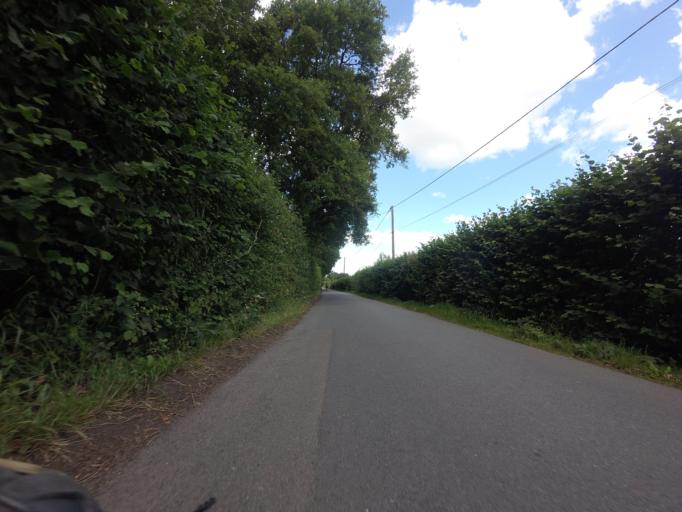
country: GB
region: England
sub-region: East Sussex
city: Hailsham
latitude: 50.8666
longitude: 0.1560
